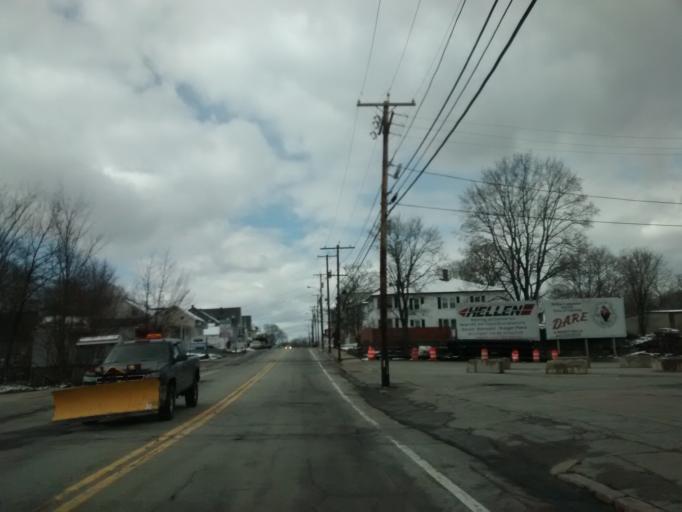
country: US
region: Massachusetts
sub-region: Worcester County
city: Uxbridge
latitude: 42.0883
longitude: -71.6417
